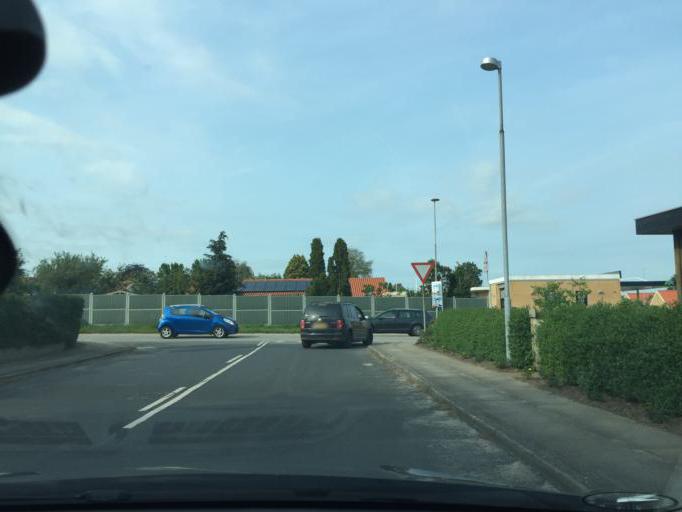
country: DK
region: South Denmark
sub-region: Odense Kommune
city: Bellinge
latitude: 55.3329
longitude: 10.3214
